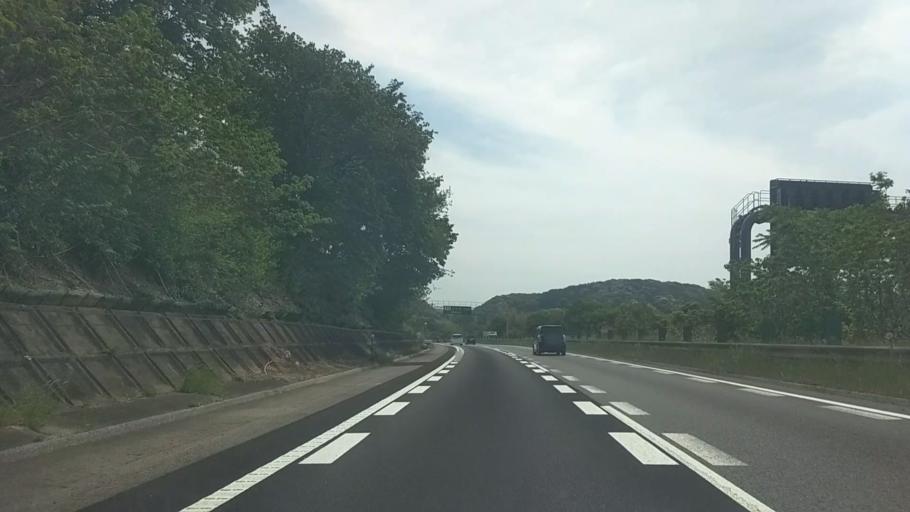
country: JP
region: Shizuoka
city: Kosai-shi
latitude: 34.8085
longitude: 137.5591
